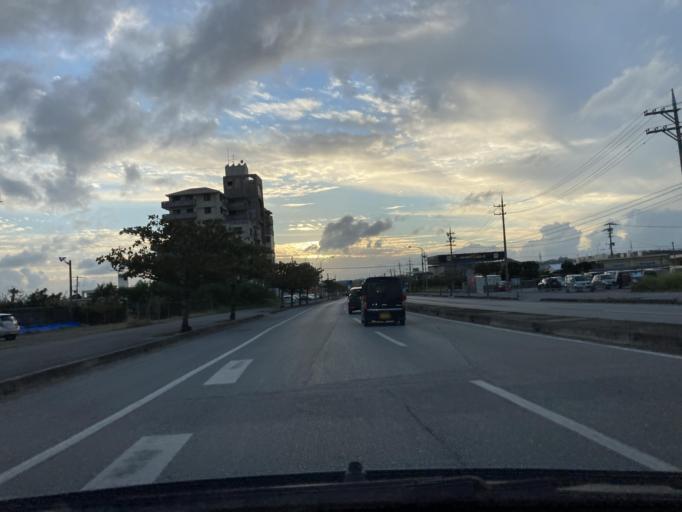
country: JP
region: Okinawa
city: Gushikawa
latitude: 26.3450
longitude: 127.8600
